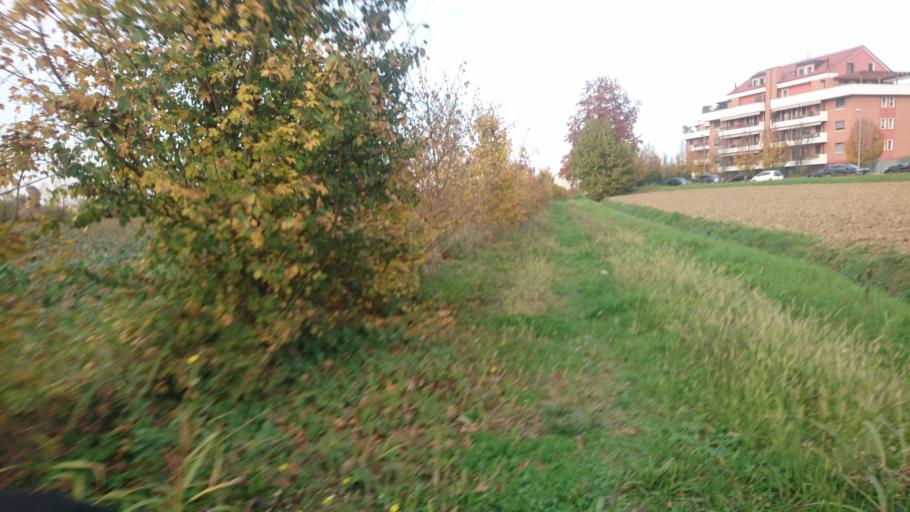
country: IT
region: Veneto
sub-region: Provincia di Padova
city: Mandriola-Sant'Agostino
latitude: 45.3824
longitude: 11.8453
